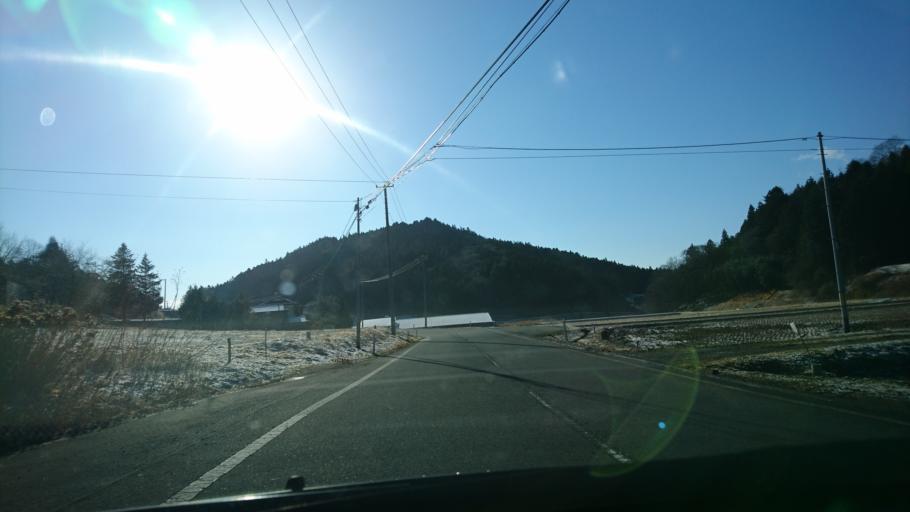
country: JP
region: Iwate
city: Ichinoseki
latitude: 38.8792
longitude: 141.3199
